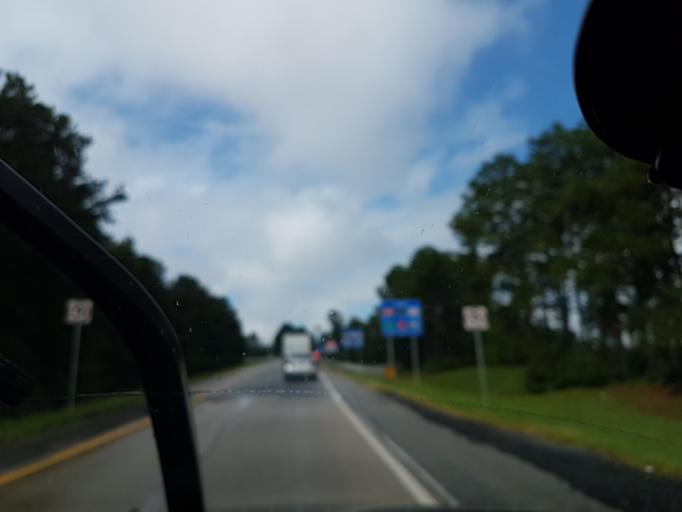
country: US
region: Georgia
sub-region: Fulton County
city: Union City
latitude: 33.5697
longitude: -84.5320
